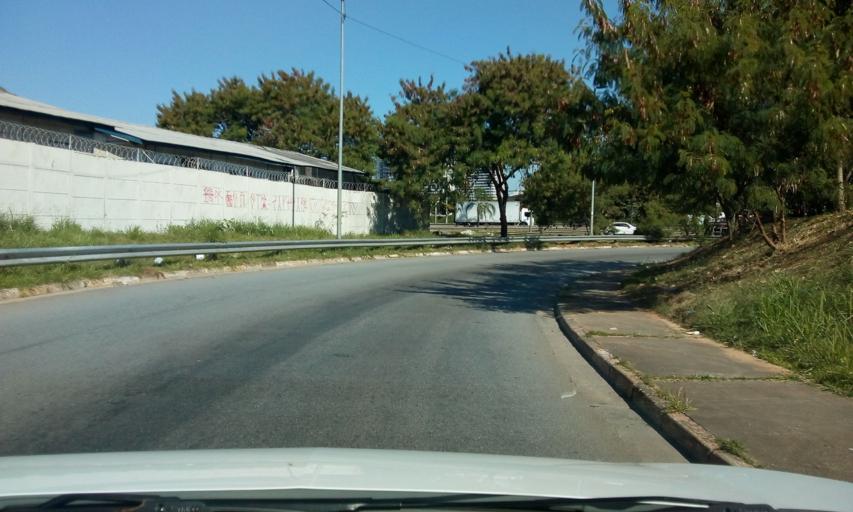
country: BR
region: Sao Paulo
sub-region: Sao Paulo
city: Sao Paulo
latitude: -23.5120
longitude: -46.6777
